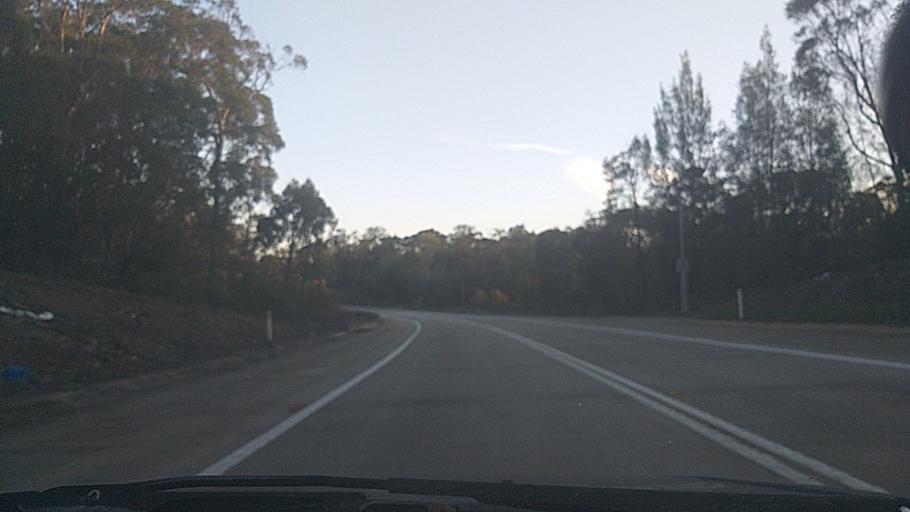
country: AU
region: New South Wales
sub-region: Wollondilly
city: Douglas Park
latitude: -34.2532
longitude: 150.7045
